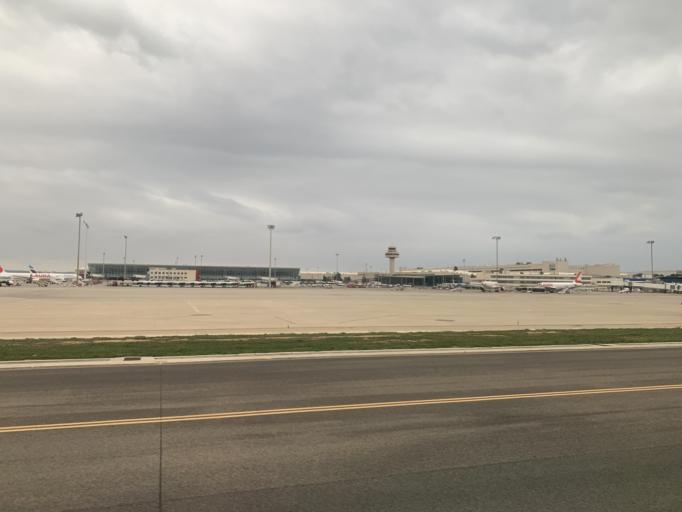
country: ES
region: Balearic Islands
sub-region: Illes Balears
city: s'Arenal
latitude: 39.5556
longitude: 2.7310
